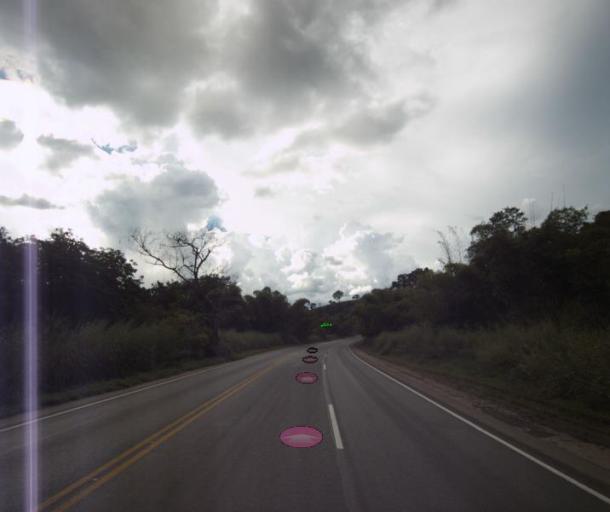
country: BR
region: Goias
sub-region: Rialma
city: Rialma
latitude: -15.2503
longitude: -49.5559
